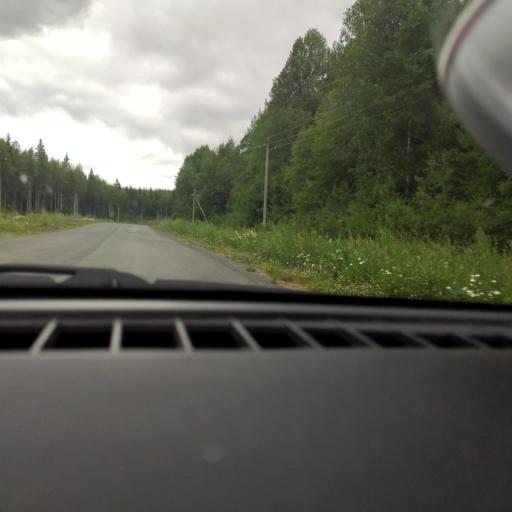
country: RU
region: Perm
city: Polazna
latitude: 58.3276
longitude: 56.1503
